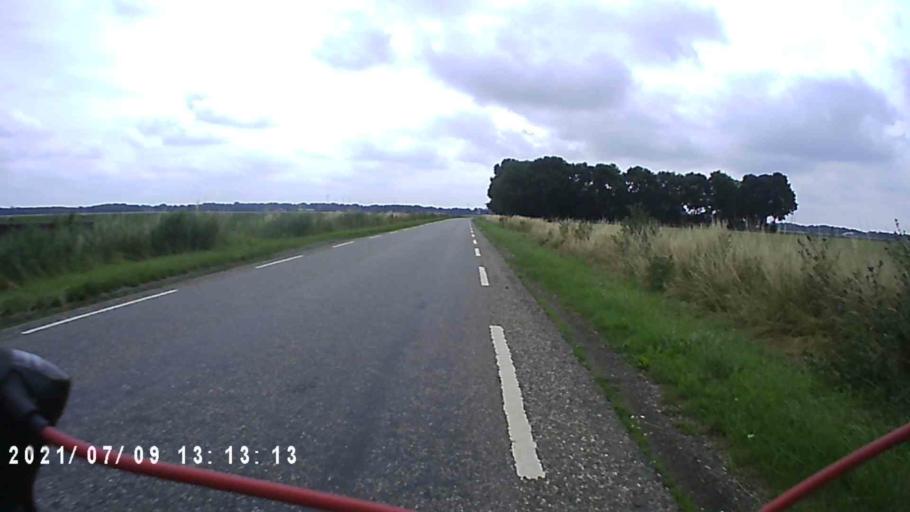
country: NL
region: Groningen
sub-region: Gemeente Vlagtwedde
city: Vlagtwedde
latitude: 53.1226
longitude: 7.1413
